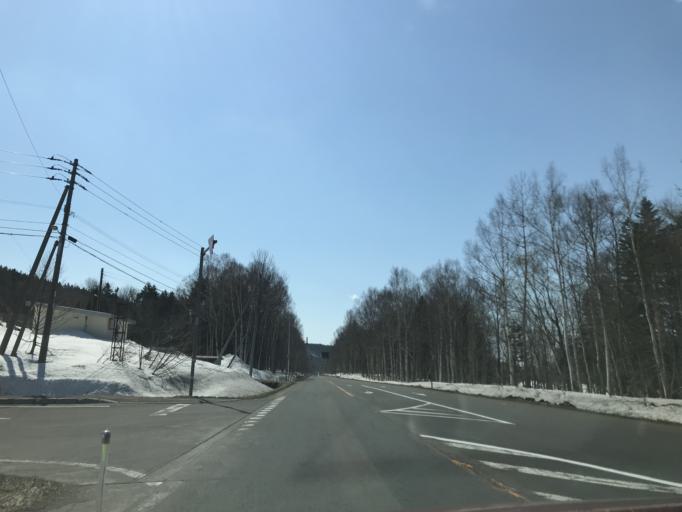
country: JP
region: Hokkaido
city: Nayoro
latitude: 44.7191
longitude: 142.2710
